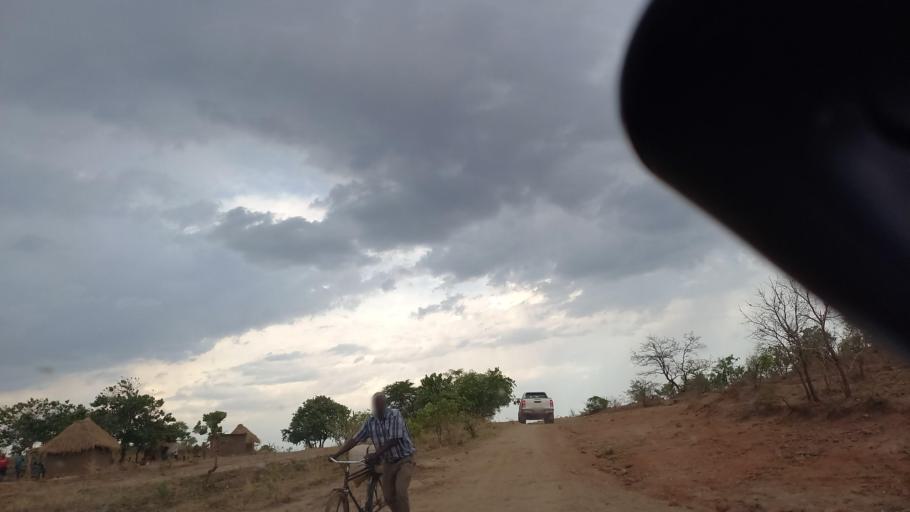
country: ZM
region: Lusaka
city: Kafue
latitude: -16.1227
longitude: 28.0616
